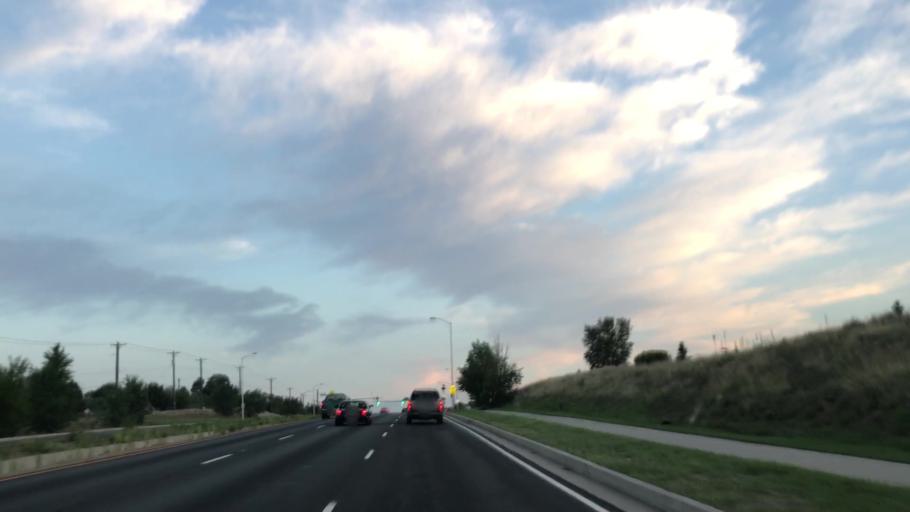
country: US
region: Colorado
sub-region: El Paso County
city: Stratmoor
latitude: 38.8132
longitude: -104.7803
